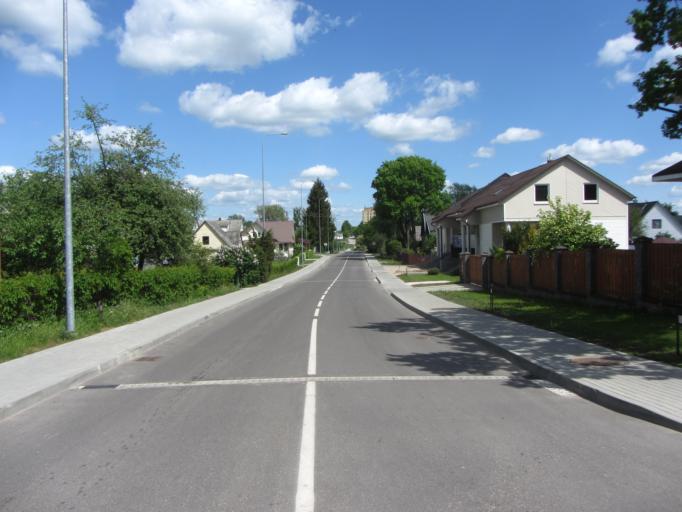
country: LT
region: Utenos apskritis
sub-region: Utena
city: Utena
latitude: 55.4994
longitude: 25.5908
